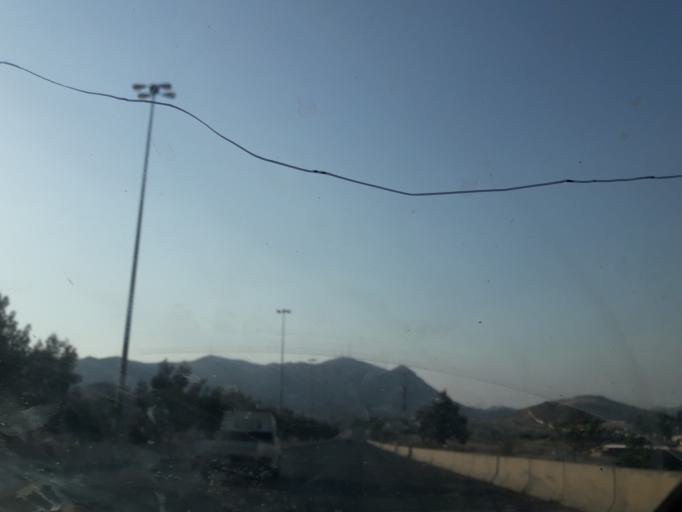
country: SA
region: Makkah
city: Ta'if
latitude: 21.2699
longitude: 40.3709
